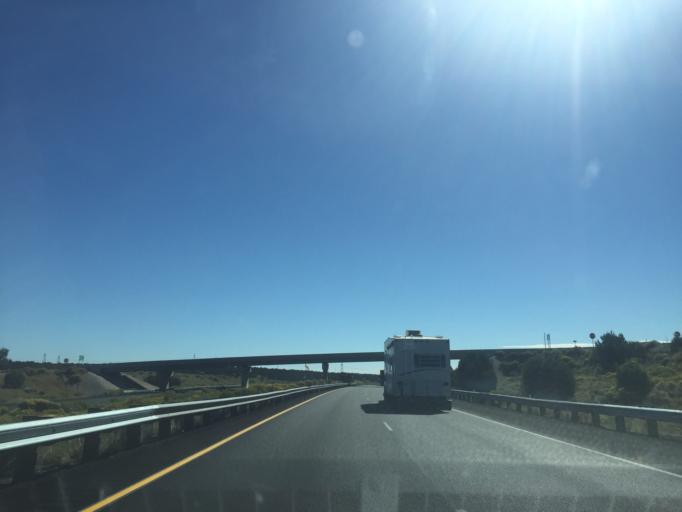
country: US
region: Arizona
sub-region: Coconino County
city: Flagstaff
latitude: 35.2020
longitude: -111.4089
